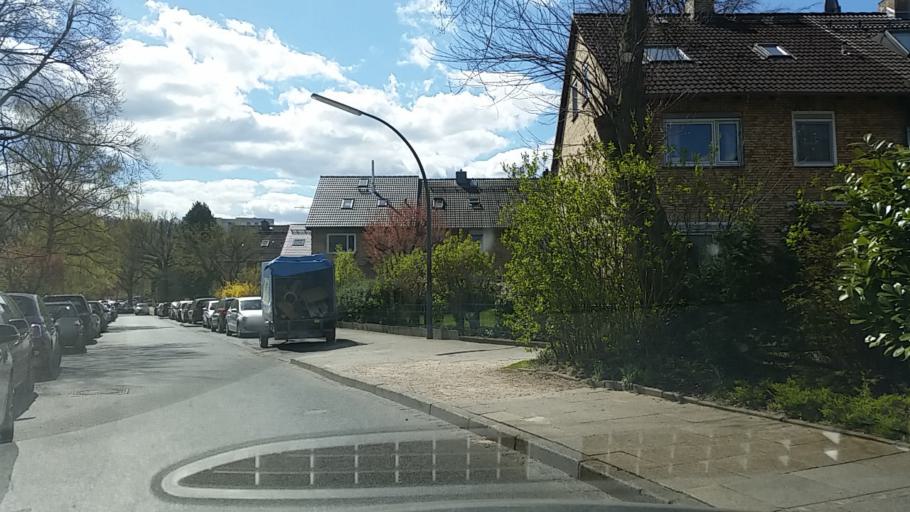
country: DE
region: Schleswig-Holstein
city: Halstenbek
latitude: 53.5732
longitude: 9.8327
